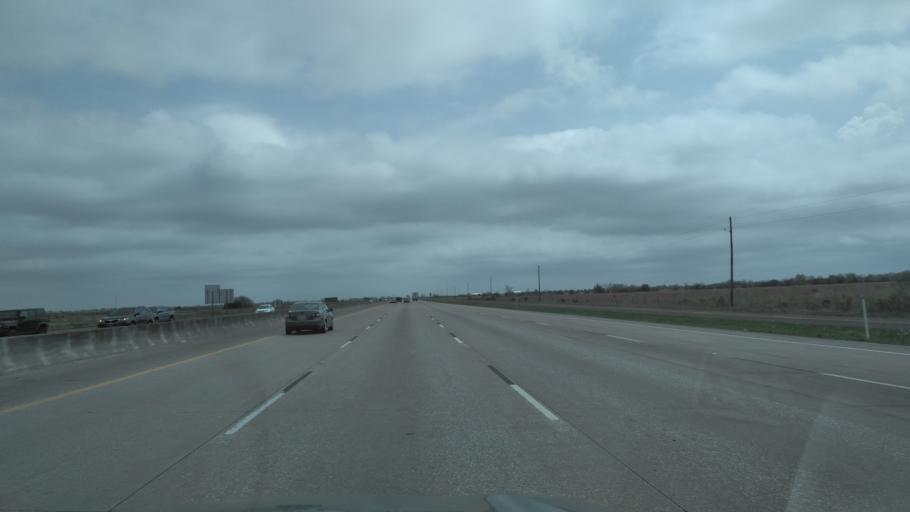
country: US
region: Texas
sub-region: Chambers County
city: Winnie
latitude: 29.8341
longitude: -94.5364
